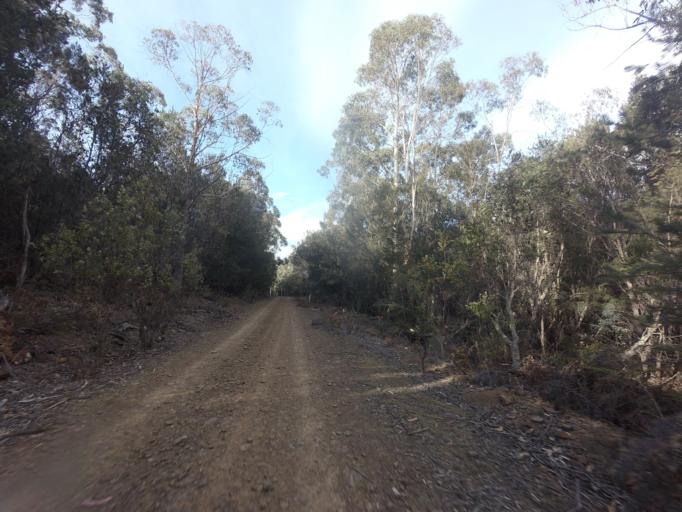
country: AU
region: Tasmania
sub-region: Break O'Day
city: St Helens
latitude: -41.8405
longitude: 148.0867
